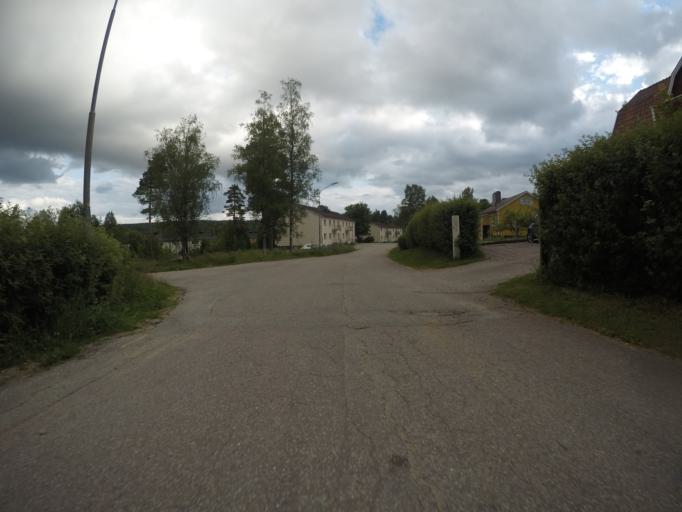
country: SE
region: Vaermland
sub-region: Filipstads Kommun
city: Lesjofors
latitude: 60.1422
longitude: 14.3882
